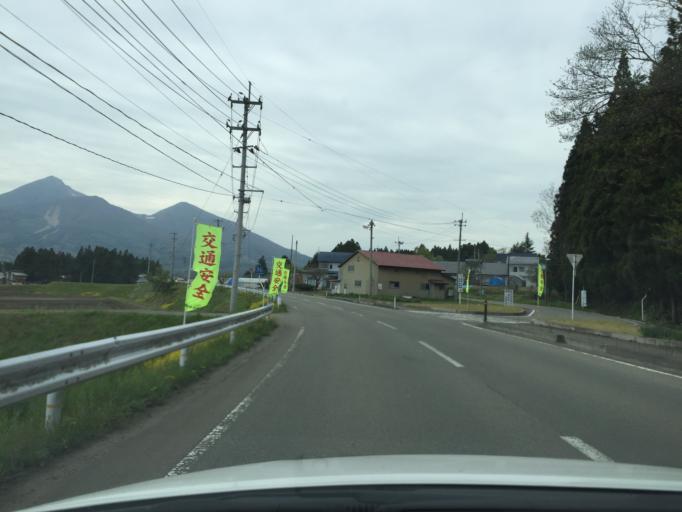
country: JP
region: Fukushima
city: Inawashiro
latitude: 37.5538
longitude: 140.1405
